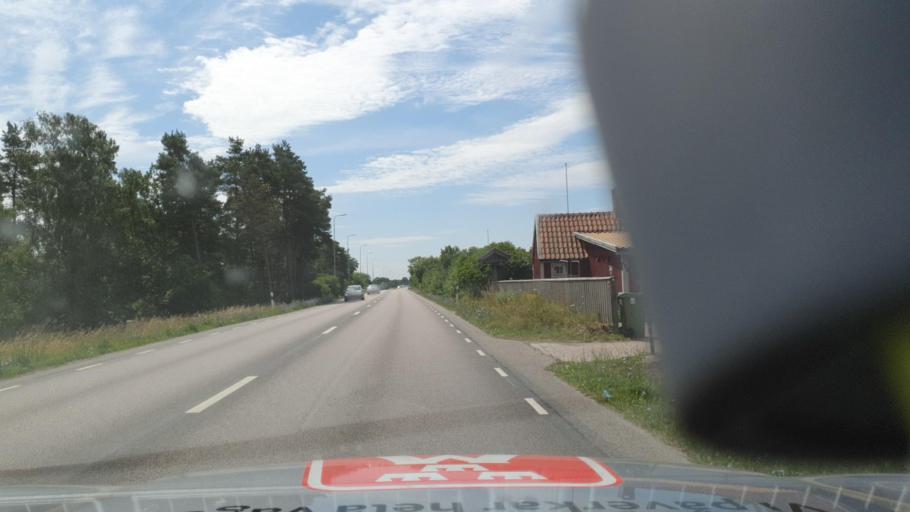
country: SE
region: Kalmar
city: Faerjestaden
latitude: 56.6943
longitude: 16.5218
